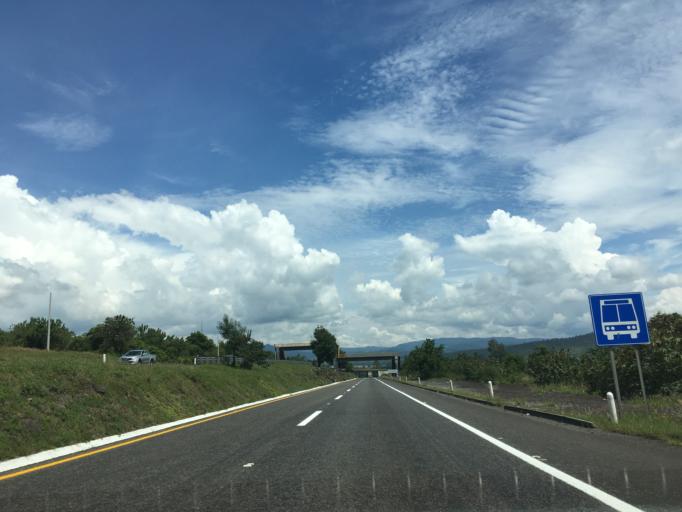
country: MX
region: Michoacan
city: Acuitzio del Canje
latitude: 19.5546
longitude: -101.3463
